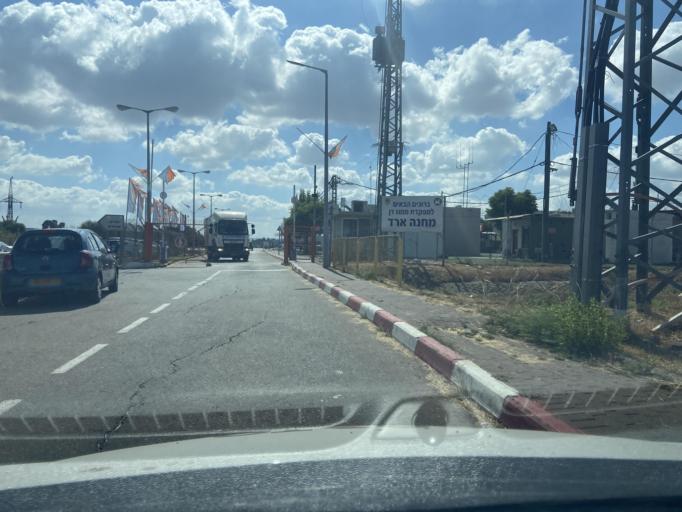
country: IL
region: Central District
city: Yehud
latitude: 32.0237
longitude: 34.8964
